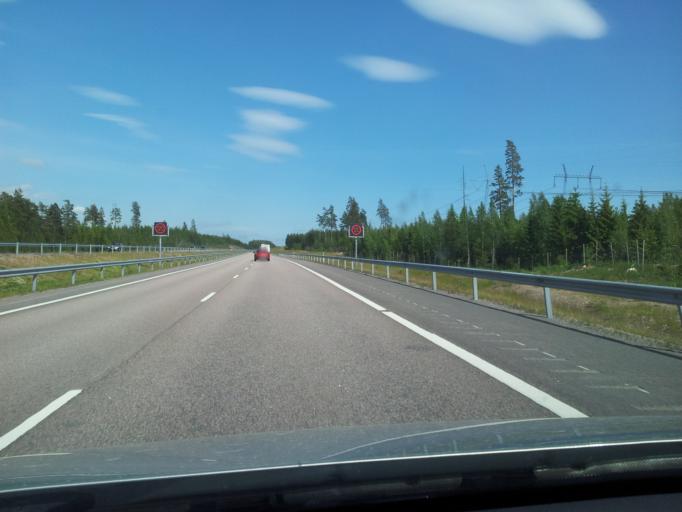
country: FI
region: Uusimaa
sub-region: Loviisa
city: Perna
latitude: 60.4776
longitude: 26.0558
